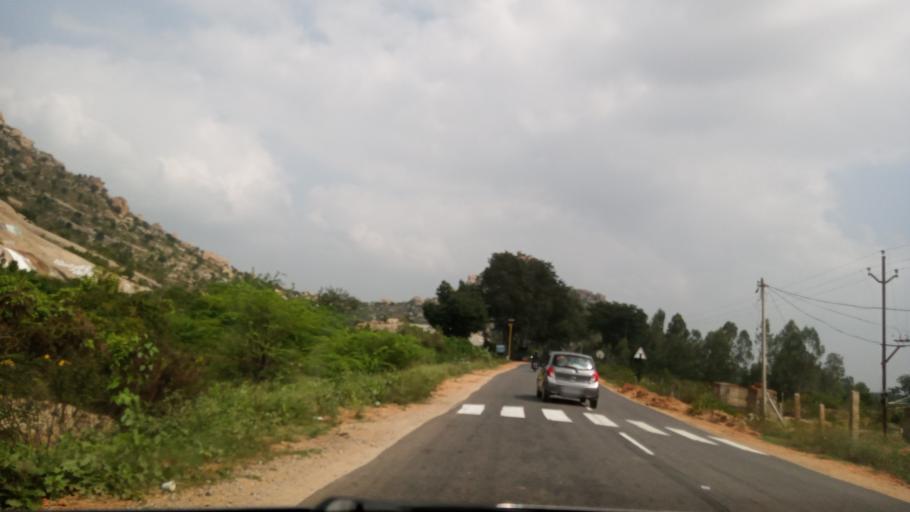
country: IN
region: Andhra Pradesh
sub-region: Chittoor
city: Madanapalle
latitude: 13.6356
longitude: 78.6092
